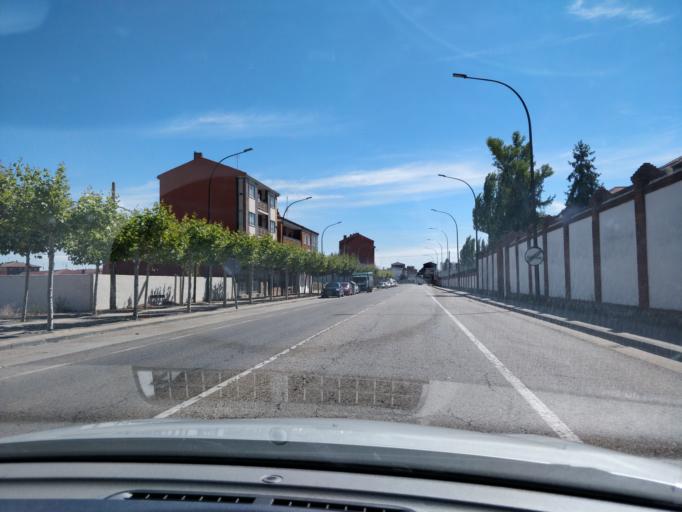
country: ES
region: Castille and Leon
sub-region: Provincia de Leon
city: Astorga
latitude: 42.4619
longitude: -6.0680
